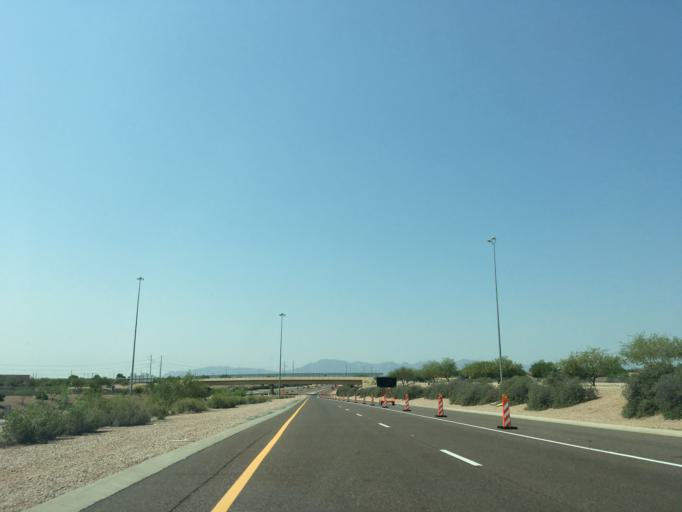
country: US
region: Arizona
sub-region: Maricopa County
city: Guadalupe
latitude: 33.2966
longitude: -111.9772
